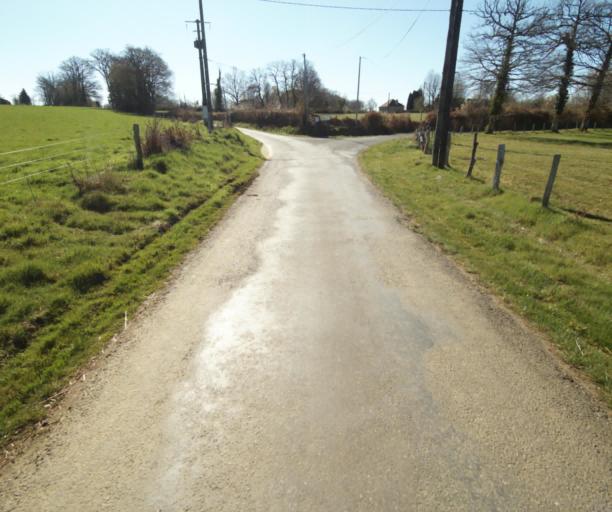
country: FR
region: Limousin
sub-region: Departement de la Correze
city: Chamboulive
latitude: 45.4075
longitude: 1.6976
